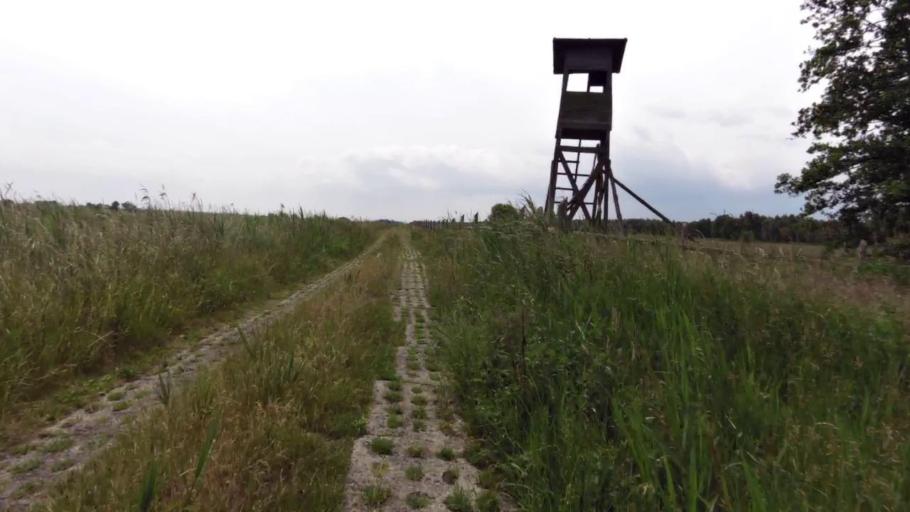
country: PL
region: West Pomeranian Voivodeship
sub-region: Powiat goleniowski
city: Stepnica
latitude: 53.7283
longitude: 14.6043
